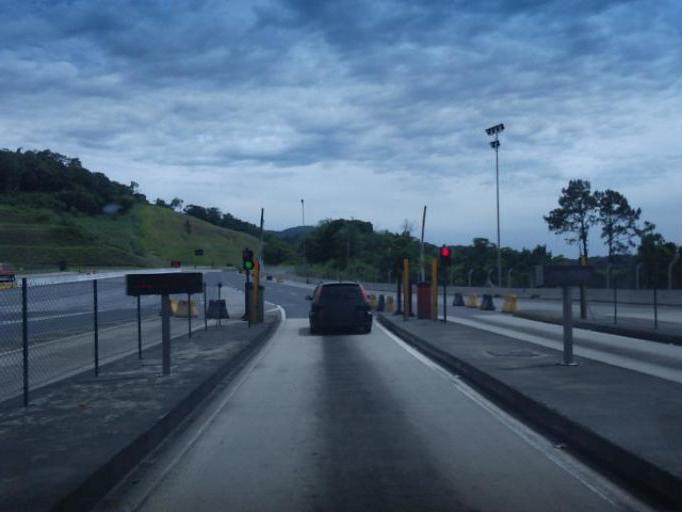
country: BR
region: Sao Paulo
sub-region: Miracatu
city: Miracatu
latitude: -24.1578
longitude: -47.3267
